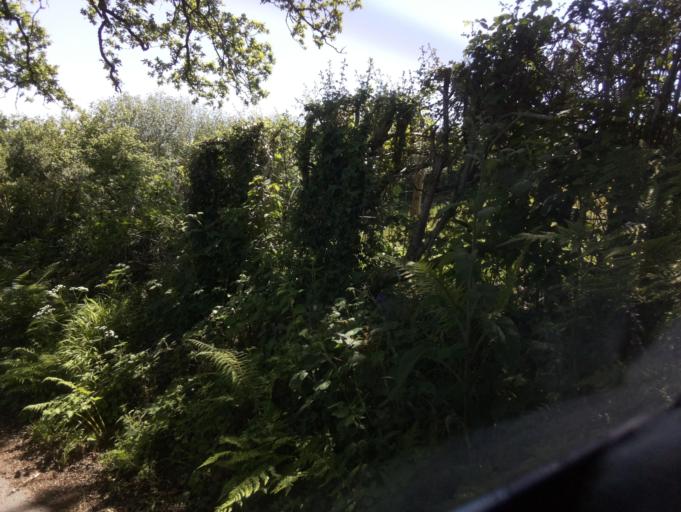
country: GB
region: Wales
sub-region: Monmouthshire
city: Llangwm
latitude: 51.6709
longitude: -2.7677
